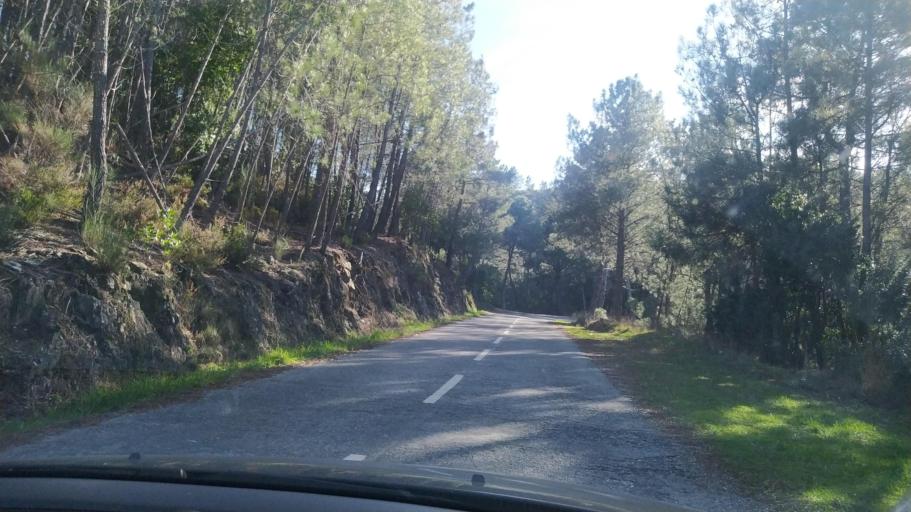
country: PT
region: Coimbra
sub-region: Oliveira do Hospital
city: Oliveira do Hospital
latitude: 40.2024
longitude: -7.7270
